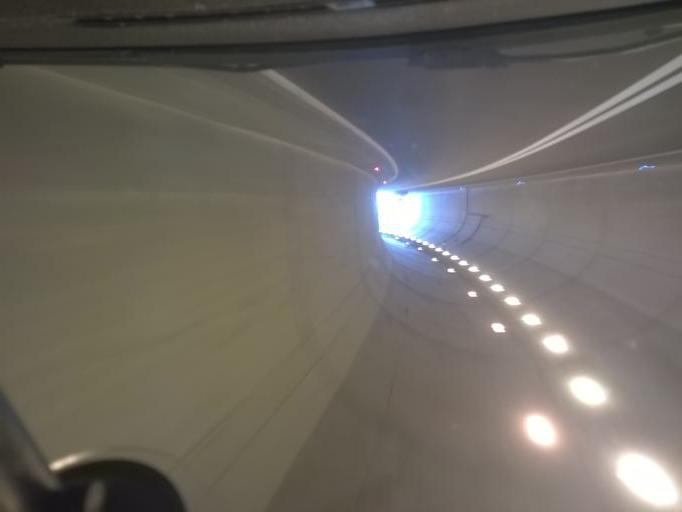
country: HR
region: Krapinsko-Zagorska
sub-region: Grad Krapina
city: Krapina
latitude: 46.1850
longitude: 15.8550
